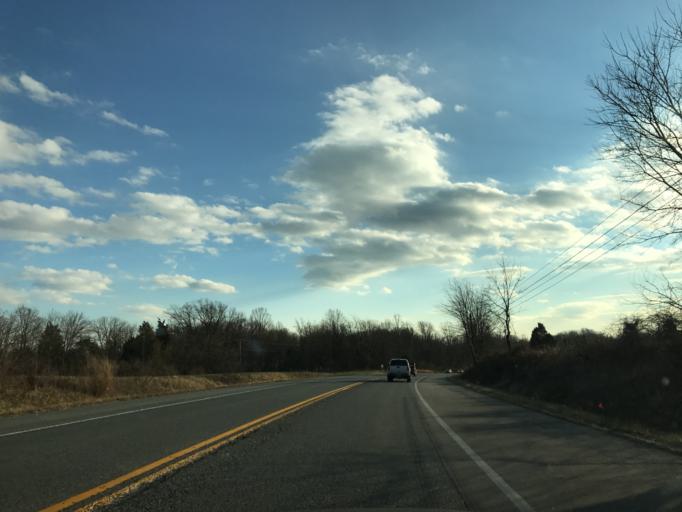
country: US
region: Maryland
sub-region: Cecil County
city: North East
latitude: 39.6530
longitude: -75.9529
